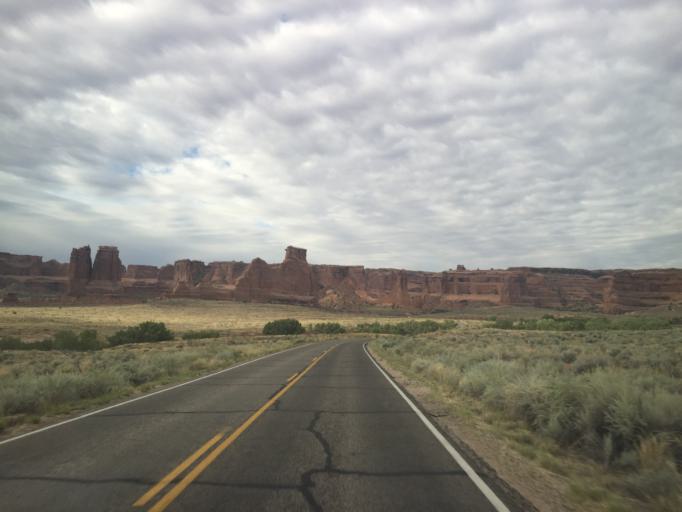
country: US
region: Utah
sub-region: Grand County
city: Moab
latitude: 38.6515
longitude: -109.5959
